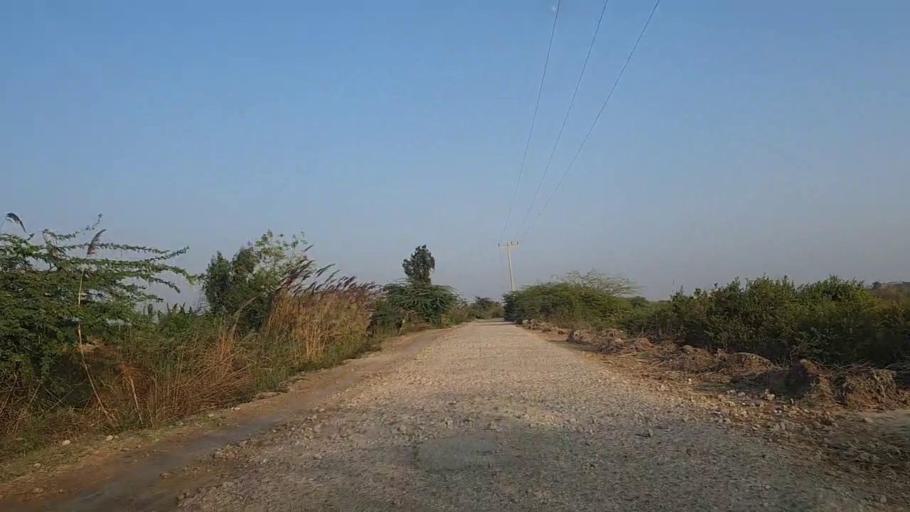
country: PK
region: Sindh
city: Keti Bandar
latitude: 24.2767
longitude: 67.6581
